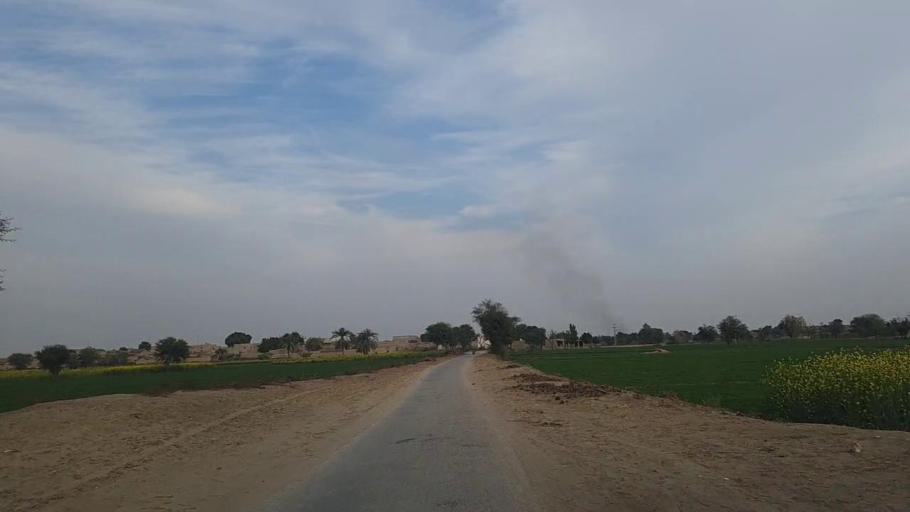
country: PK
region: Sindh
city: Daur
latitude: 26.5288
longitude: 68.4205
